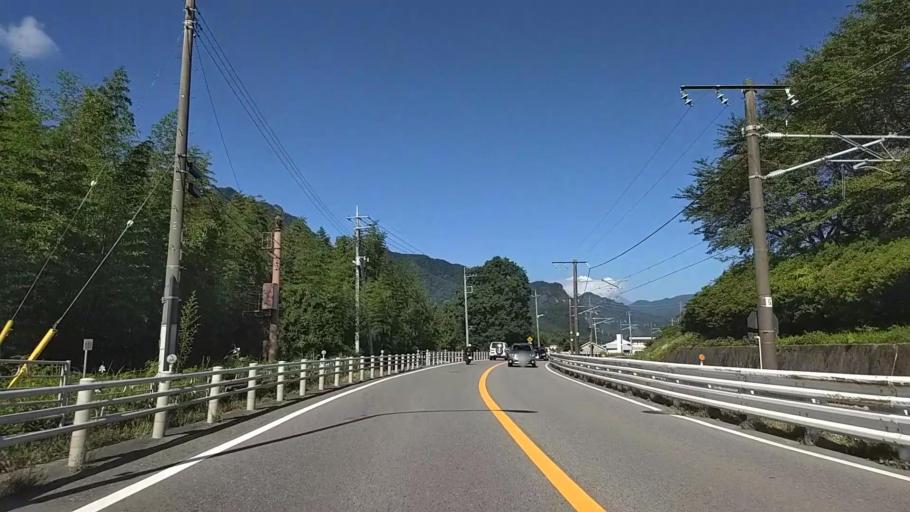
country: JP
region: Gunma
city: Annaka
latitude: 36.3257
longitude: 138.7600
